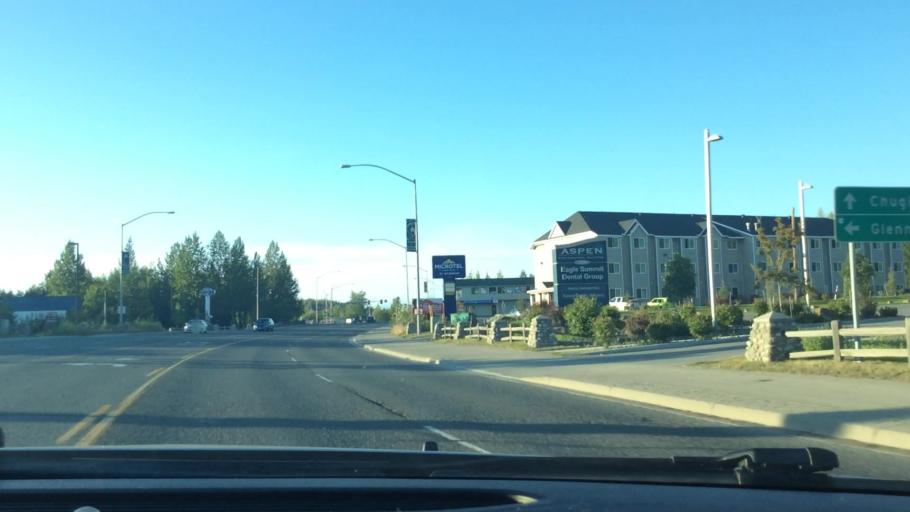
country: US
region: Alaska
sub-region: Anchorage Municipality
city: Eagle River
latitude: 61.3378
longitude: -149.5631
